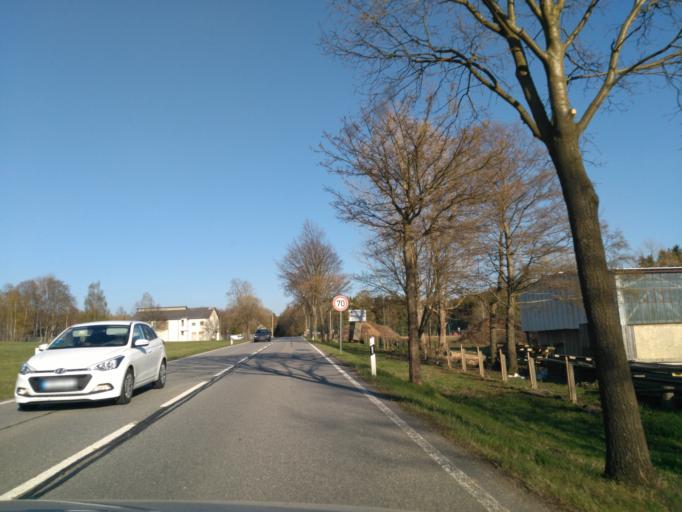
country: DE
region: Saxony
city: Schlettau
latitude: 50.5541
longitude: 12.9787
